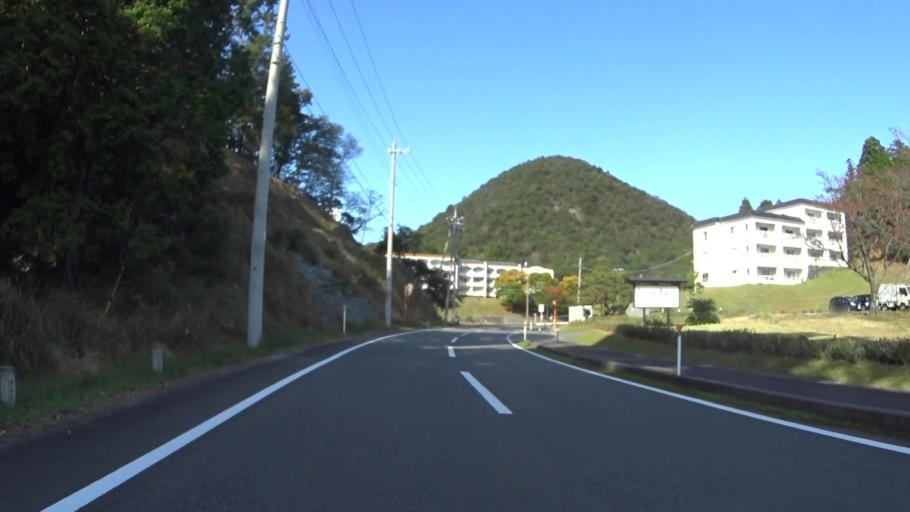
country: JP
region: Hyogo
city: Toyooka
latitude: 35.6345
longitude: 134.8886
